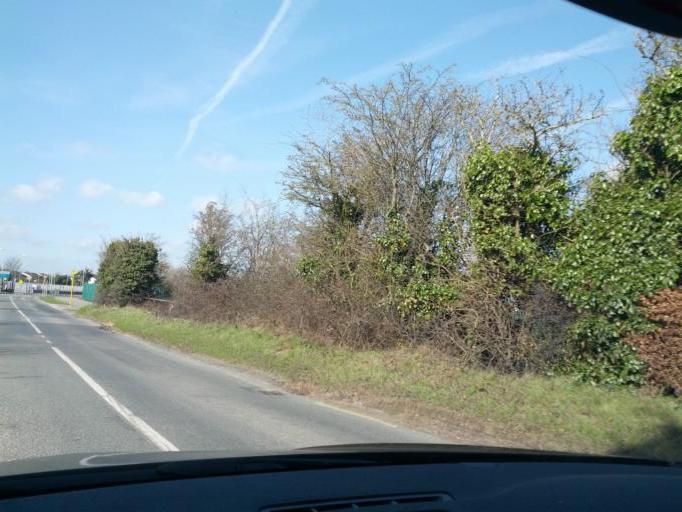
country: IE
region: Leinster
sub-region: Kildare
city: Maynooth
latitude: 53.3693
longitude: -6.5791
